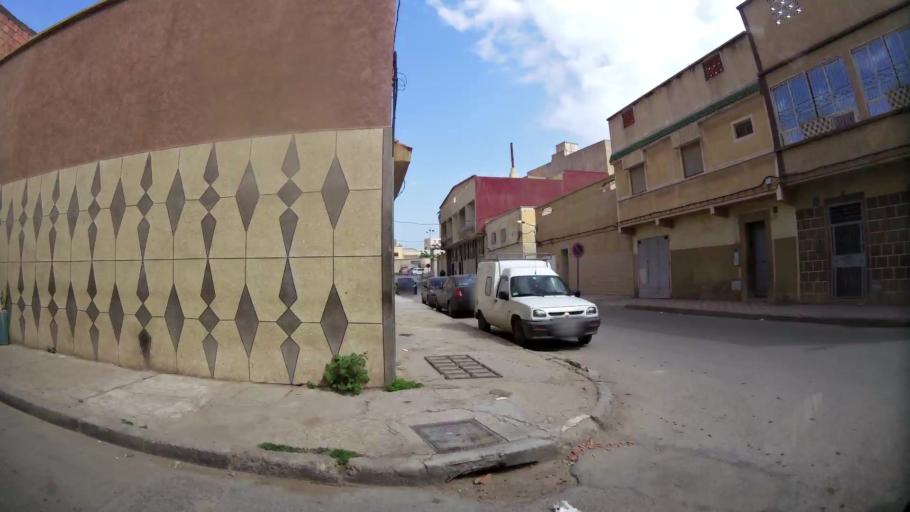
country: MA
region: Oriental
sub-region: Oujda-Angad
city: Oujda
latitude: 34.6892
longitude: -1.9086
